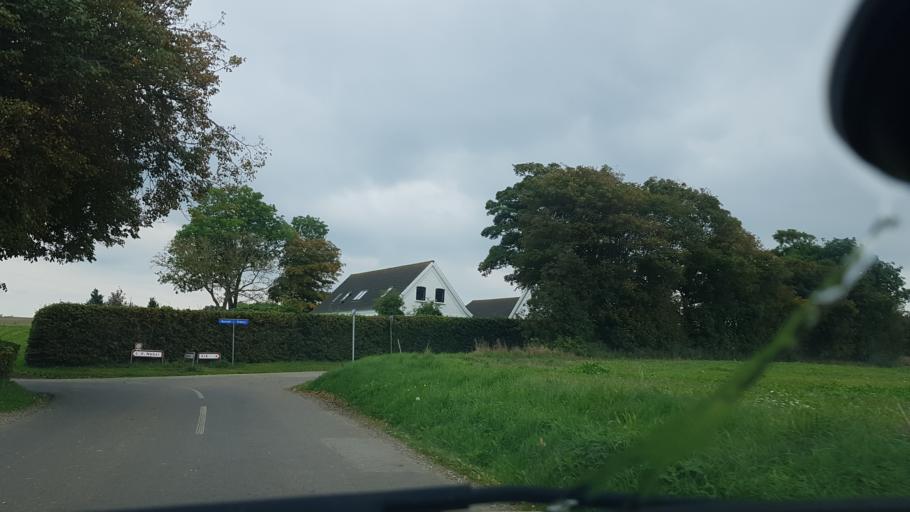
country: DK
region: South Denmark
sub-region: Vejle Kommune
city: Egtved
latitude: 55.5549
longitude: 9.3316
